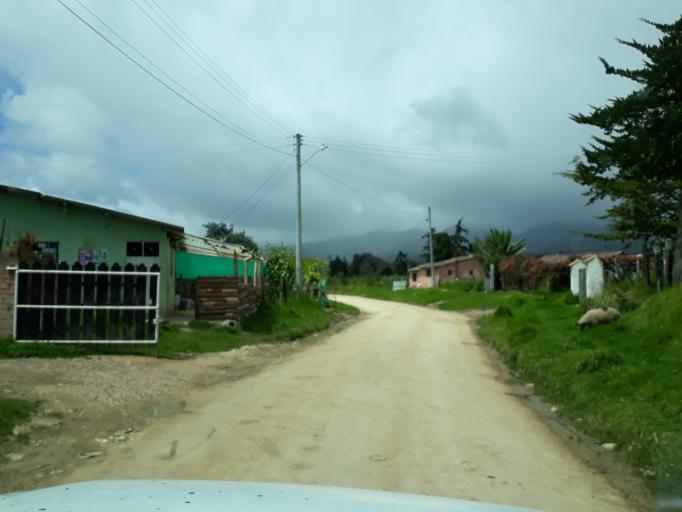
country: CO
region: Cundinamarca
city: Guasca
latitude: 4.8597
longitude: -73.8857
